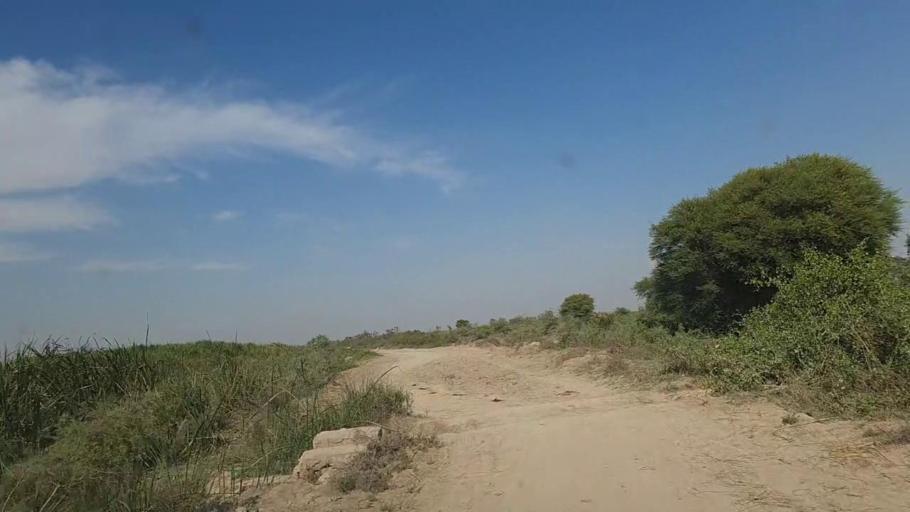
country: PK
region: Sindh
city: Mirpur Batoro
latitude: 24.7974
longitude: 68.2695
